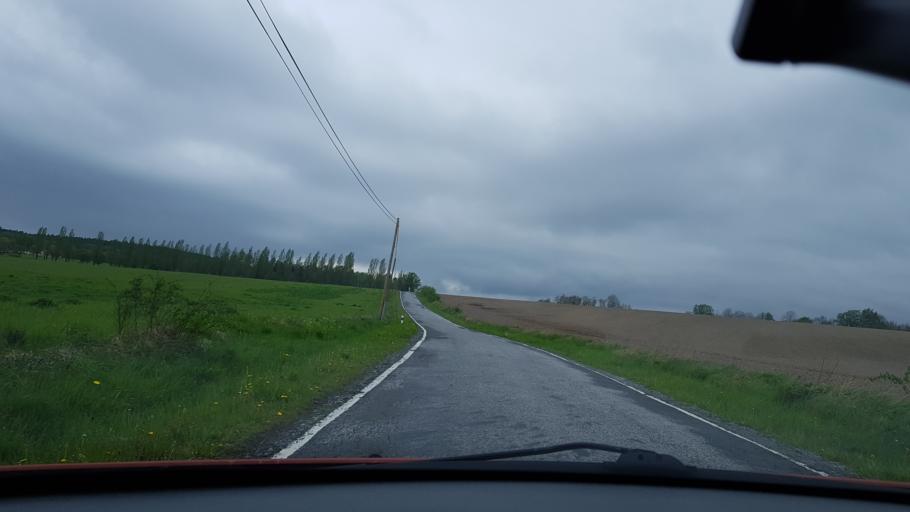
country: PL
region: Lower Silesian Voivodeship
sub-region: Powiat zabkowicki
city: Zloty Stok
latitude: 50.4436
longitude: 16.9046
